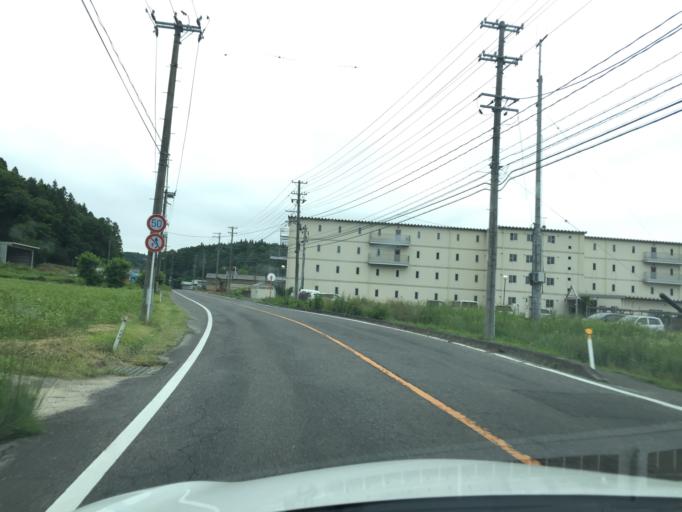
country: JP
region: Fukushima
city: Funehikimachi-funehiki
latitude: 37.3013
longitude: 140.6506
